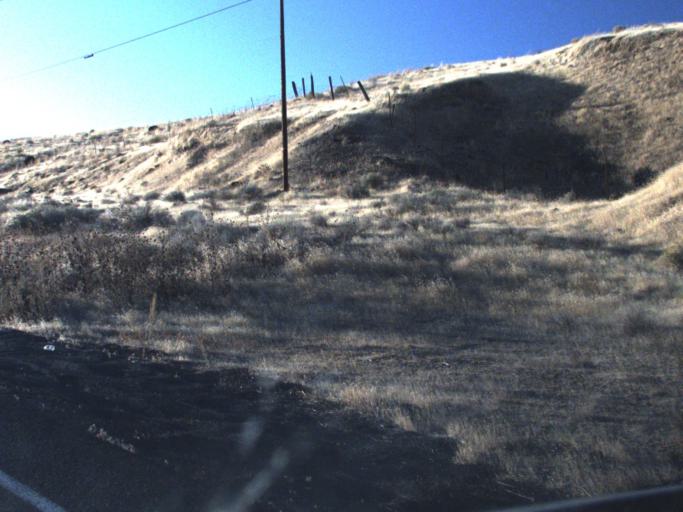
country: US
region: Washington
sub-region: Franklin County
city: Connell
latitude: 46.6504
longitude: -118.5133
